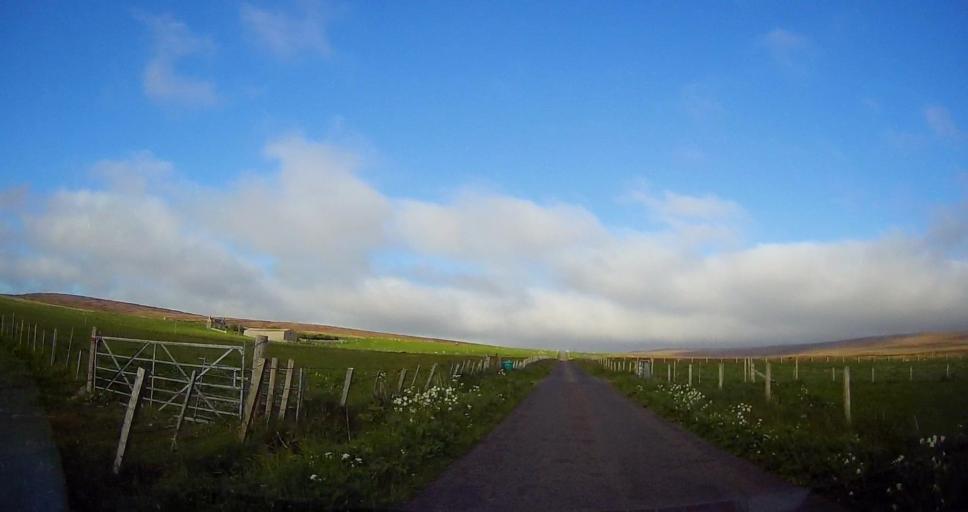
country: GB
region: Scotland
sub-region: Orkney Islands
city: Stromness
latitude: 59.0936
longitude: -3.1774
